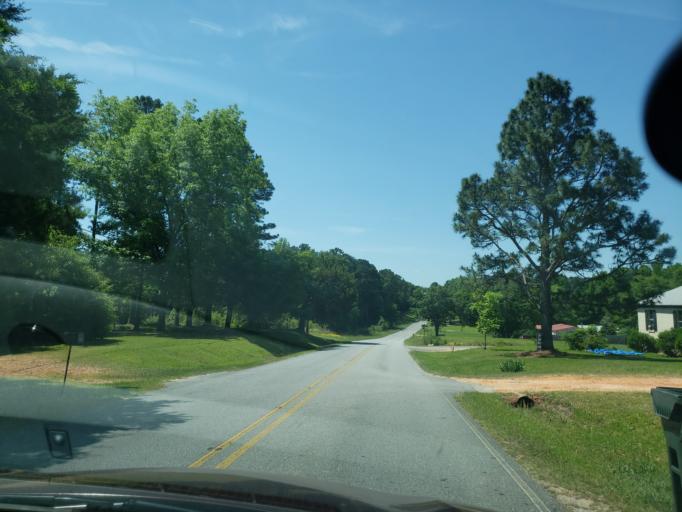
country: US
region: Alabama
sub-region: Elmore County
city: Tallassee
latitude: 32.5883
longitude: -85.8576
